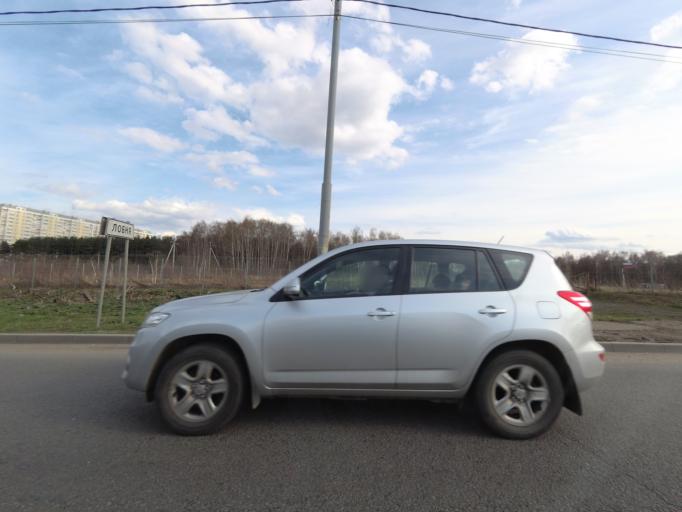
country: RU
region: Moskovskaya
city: Lobnya
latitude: 56.0045
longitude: 37.4298
